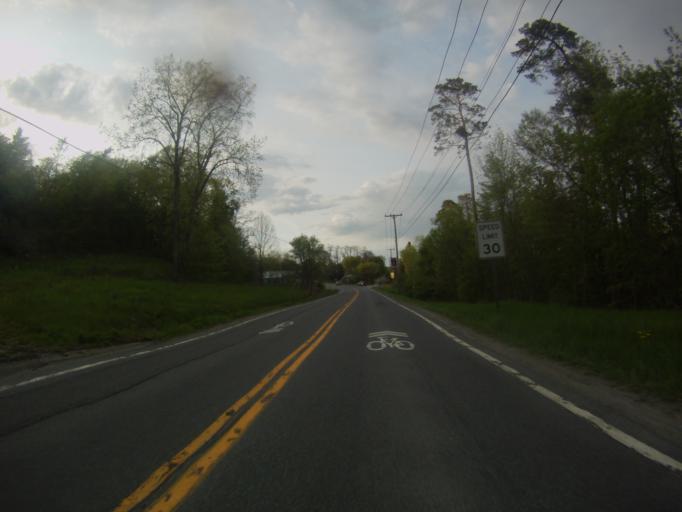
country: US
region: New York
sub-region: Essex County
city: Ticonderoga
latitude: 43.9466
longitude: -73.4177
